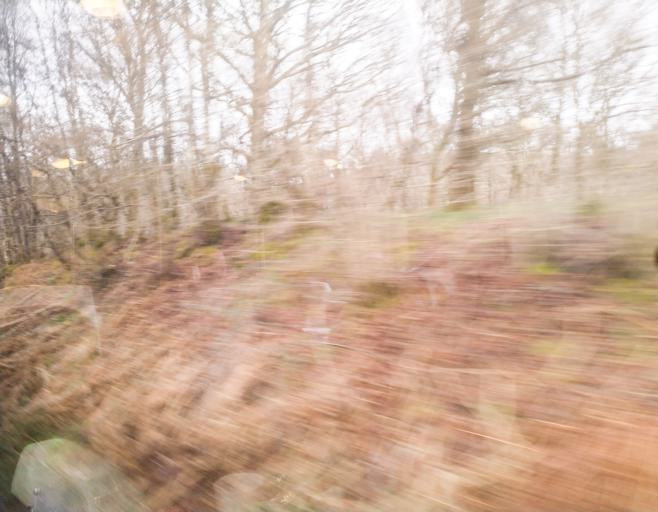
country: GB
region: Scotland
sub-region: Highland
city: Spean Bridge
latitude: 56.8901
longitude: -4.8758
